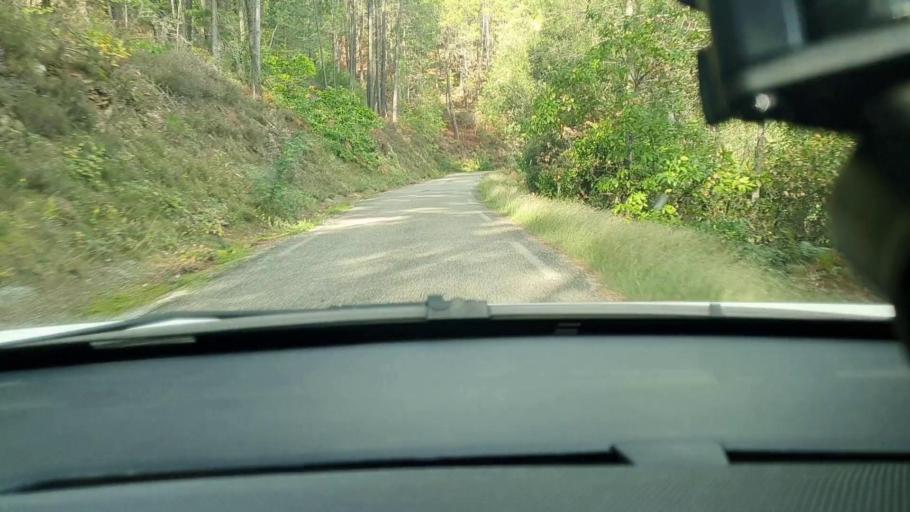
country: FR
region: Languedoc-Roussillon
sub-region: Departement du Gard
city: Besseges
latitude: 44.3215
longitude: 4.0436
